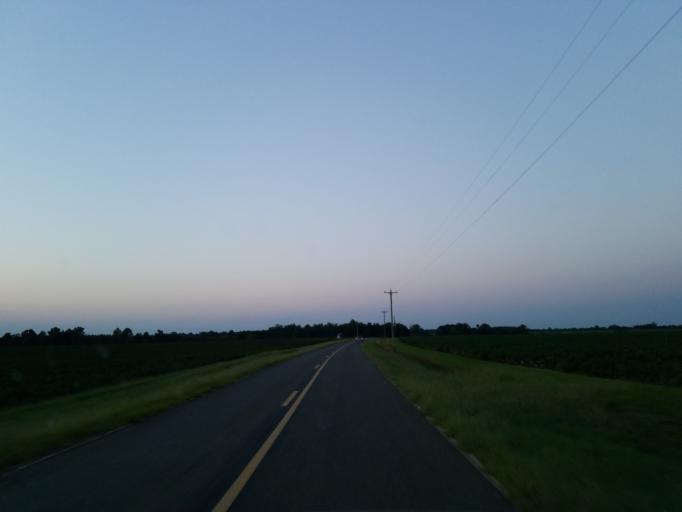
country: US
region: Georgia
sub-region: Dooly County
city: Unadilla
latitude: 32.2778
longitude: -83.7956
